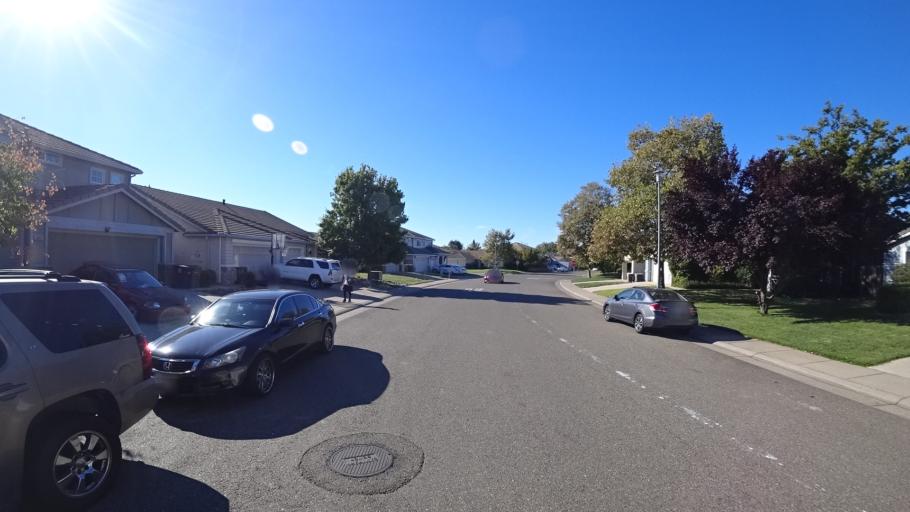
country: US
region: California
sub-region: Sacramento County
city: Vineyard
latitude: 38.4435
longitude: -121.3676
